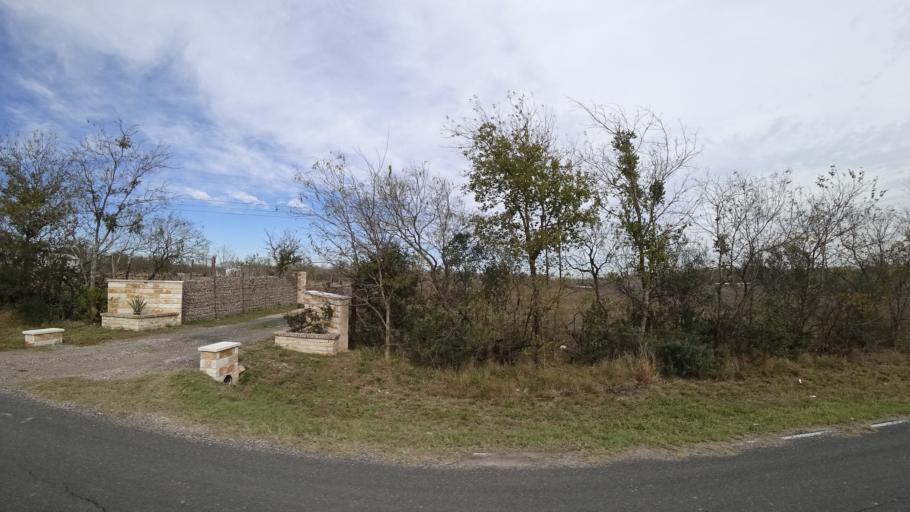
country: US
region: Texas
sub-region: Travis County
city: Garfield
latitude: 30.1405
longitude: -97.5815
